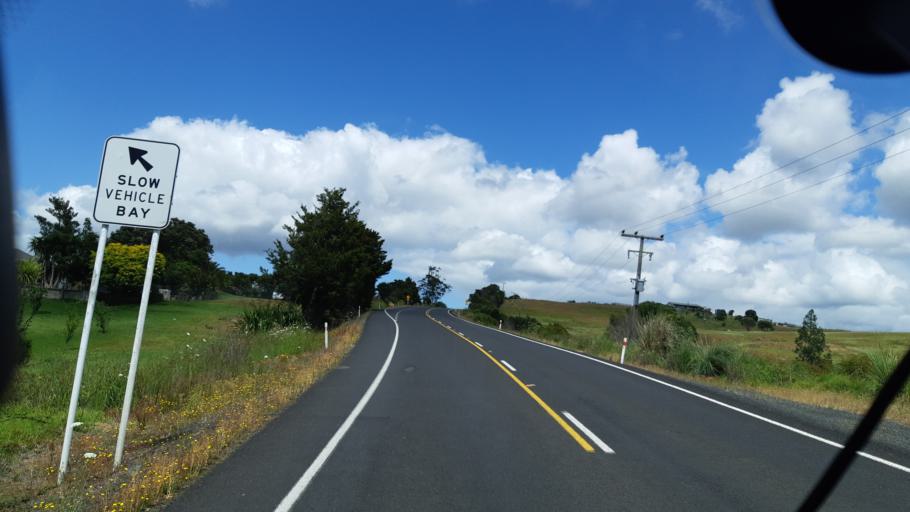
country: NZ
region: Northland
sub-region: Far North District
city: Waimate North
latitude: -35.2944
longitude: 173.6164
